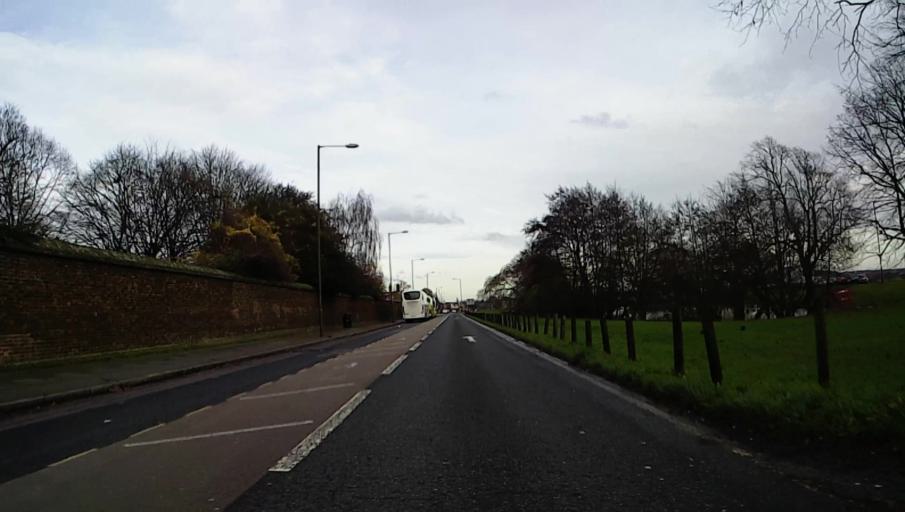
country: GB
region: England
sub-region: Greater London
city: Blackheath
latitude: 51.4723
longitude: 0.0012
